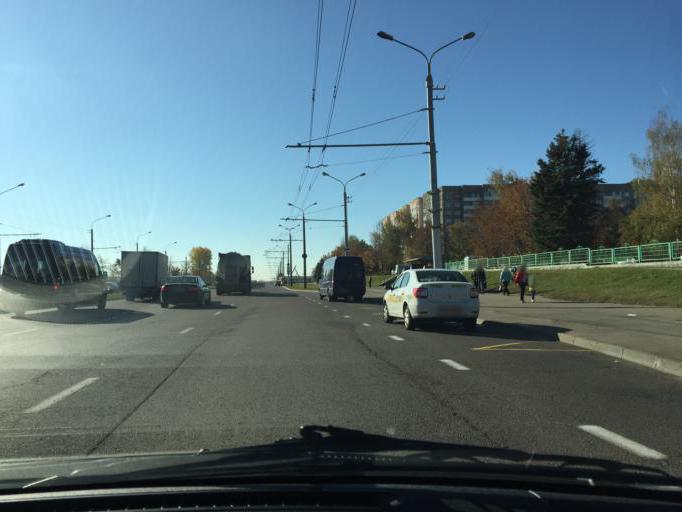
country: BY
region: Minsk
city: Syenitsa
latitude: 53.8499
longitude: 27.5365
